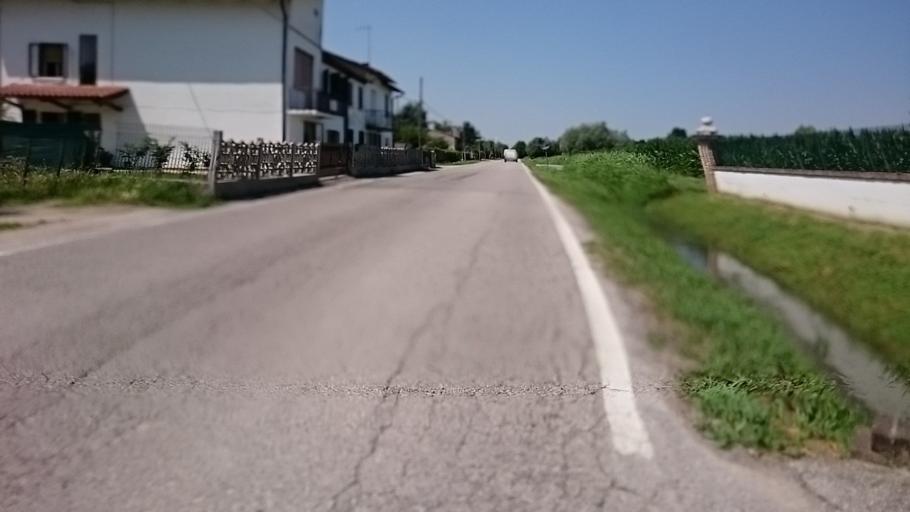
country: IT
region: Veneto
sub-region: Provincia di Venezia
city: Sant'Angelo
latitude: 45.5166
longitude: 12.0059
